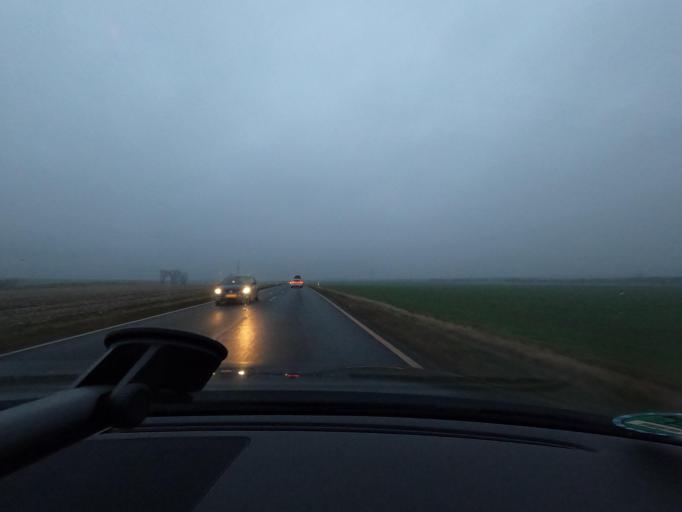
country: DE
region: Thuringia
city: Dollstadt
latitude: 51.0778
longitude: 10.8213
